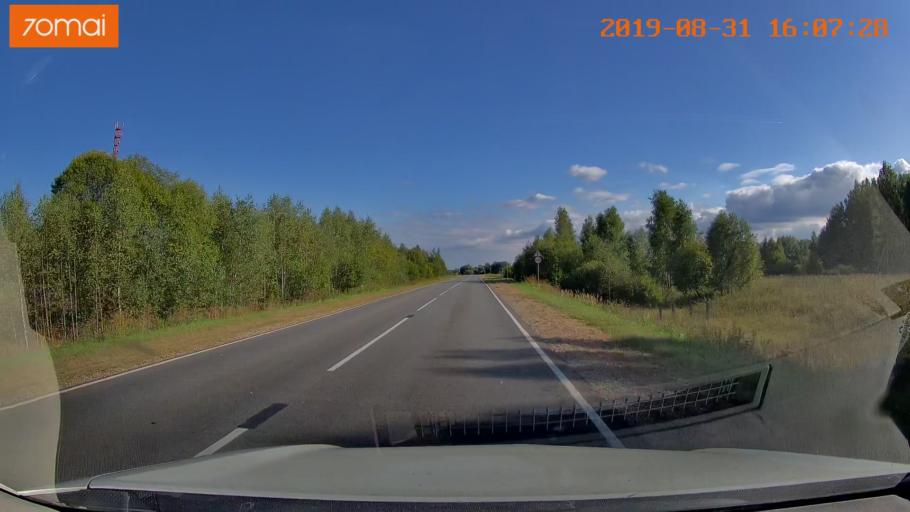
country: RU
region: Kaluga
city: Yukhnov
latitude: 54.6092
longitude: 35.3589
